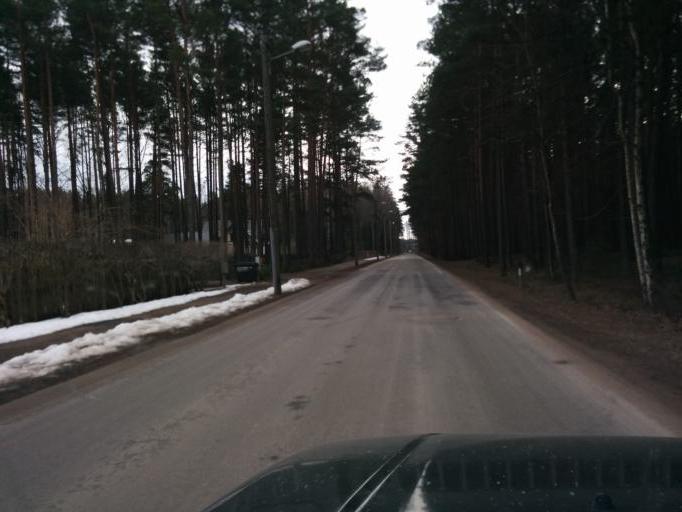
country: LV
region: Jurmala
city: Jurmala
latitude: 56.9490
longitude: 23.7256
